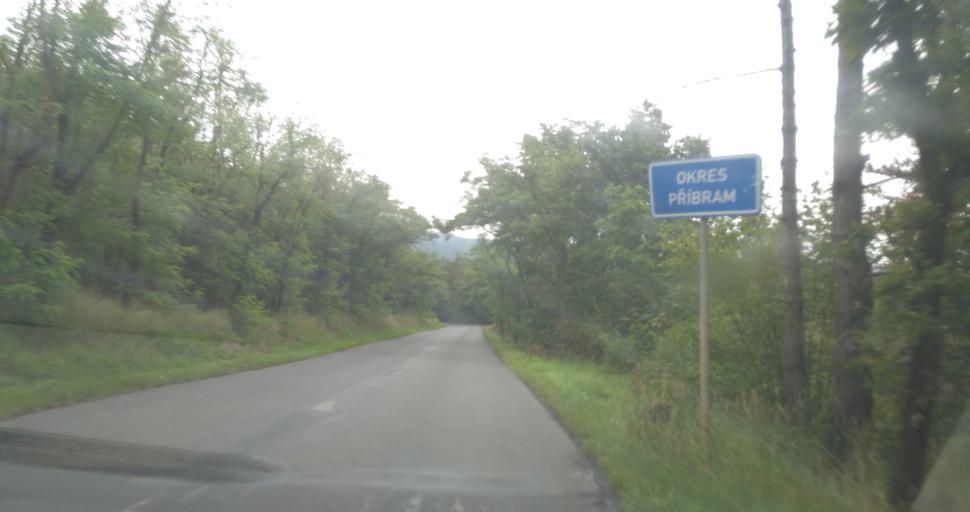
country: CZ
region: Central Bohemia
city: Jince
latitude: 49.8117
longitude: 13.9475
